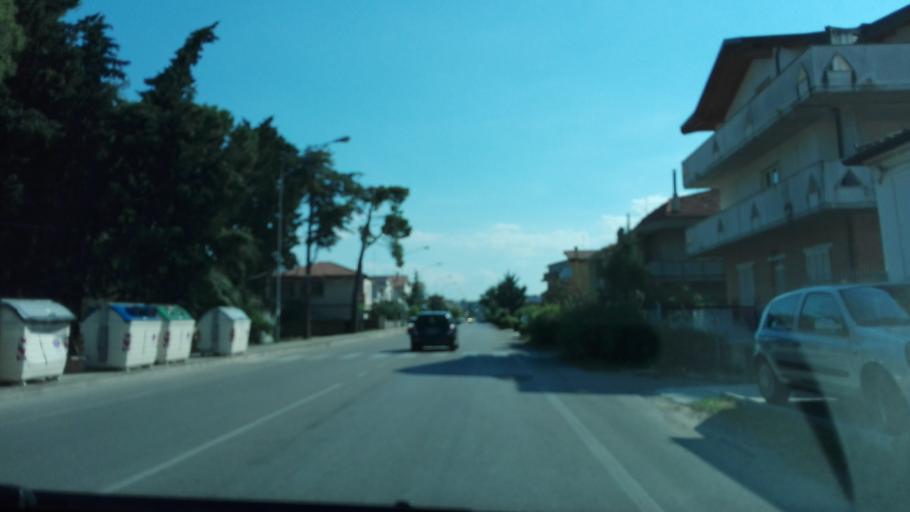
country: IT
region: Abruzzo
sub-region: Provincia di Pescara
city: Cappelle sul Tavo
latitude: 42.4879
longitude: 14.1204
